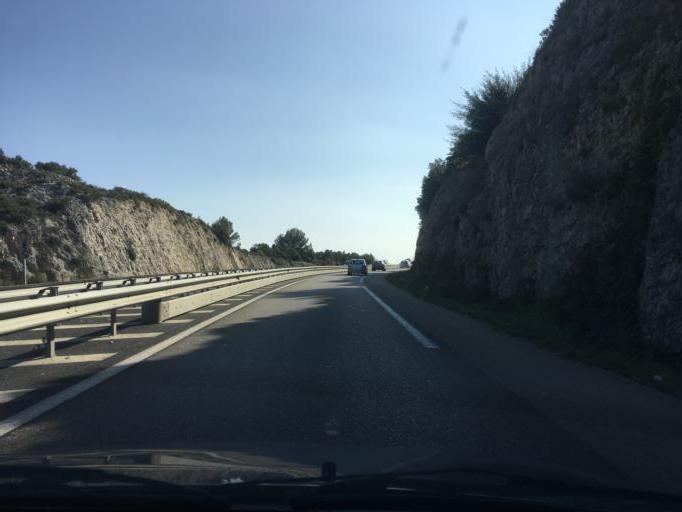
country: FR
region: Languedoc-Roussillon
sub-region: Departement du Gard
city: Les Angles
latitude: 43.9648
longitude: 4.7437
